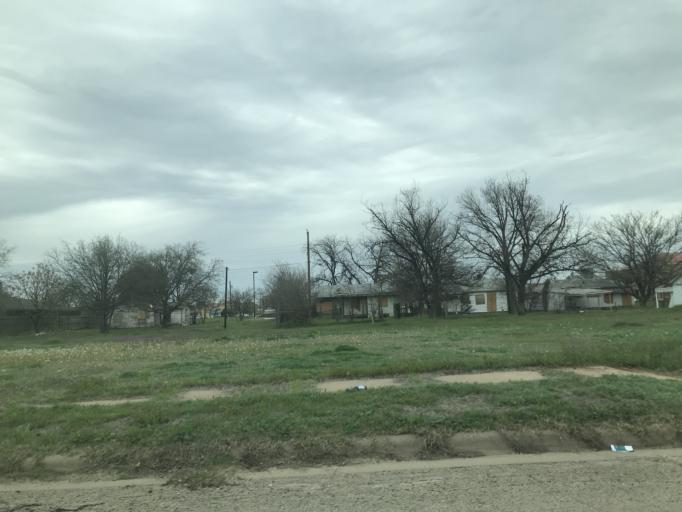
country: US
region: Texas
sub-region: Taylor County
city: Abilene
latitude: 32.4664
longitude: -99.7344
